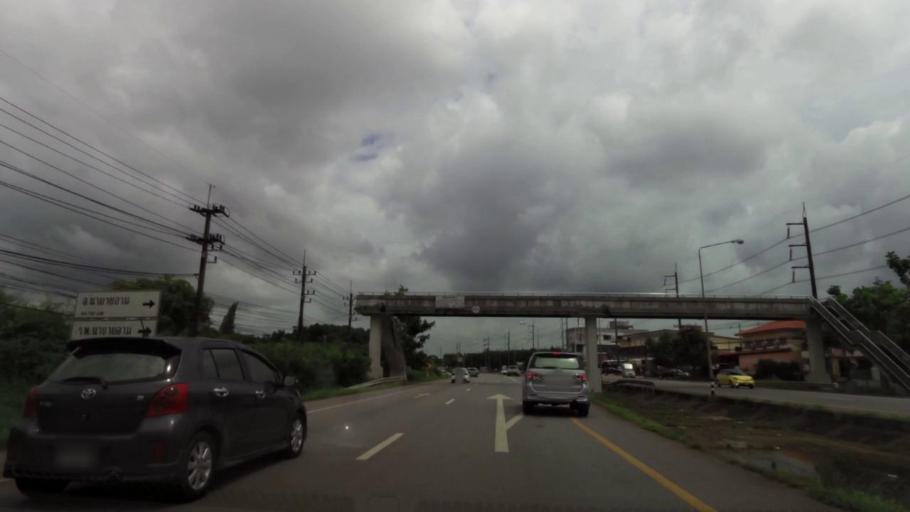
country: TH
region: Chanthaburi
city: Na Yai Am
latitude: 12.7658
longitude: 101.8513
